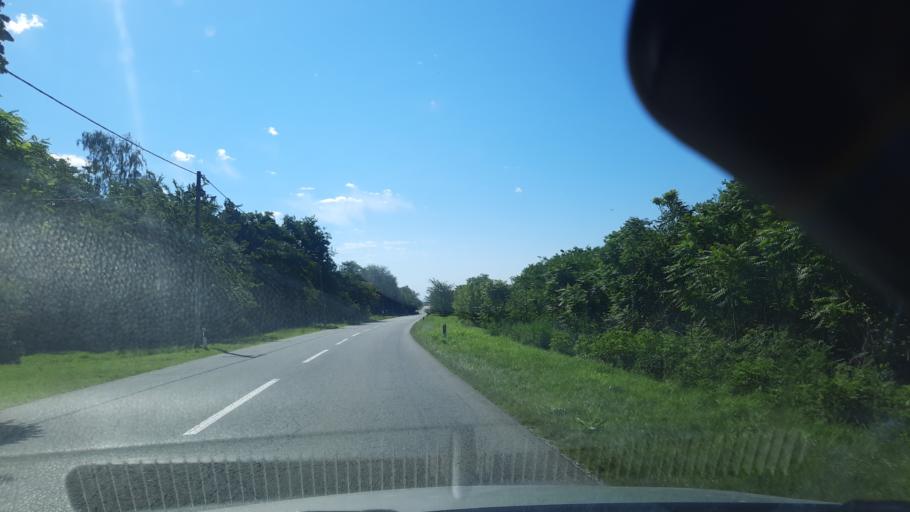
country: RS
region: Autonomna Pokrajina Vojvodina
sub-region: Juznobanatski Okrug
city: Kovin
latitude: 44.8128
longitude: 21.1582
